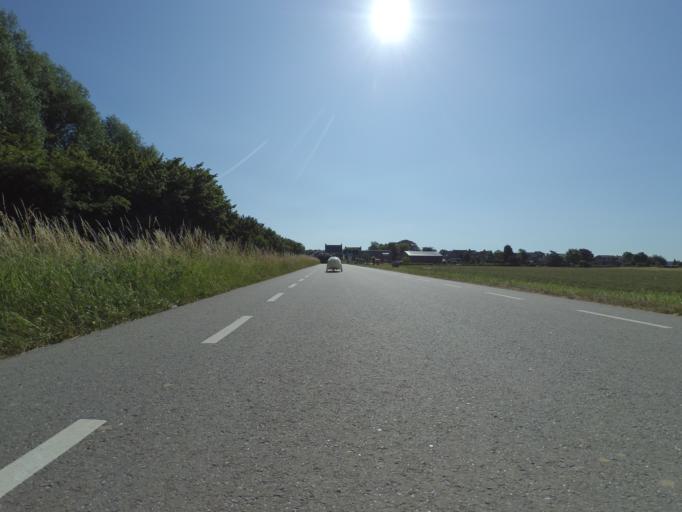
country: NL
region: North Brabant
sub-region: Gemeente Woensdrecht
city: Woensdrecht
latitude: 51.3932
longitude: 4.3114
